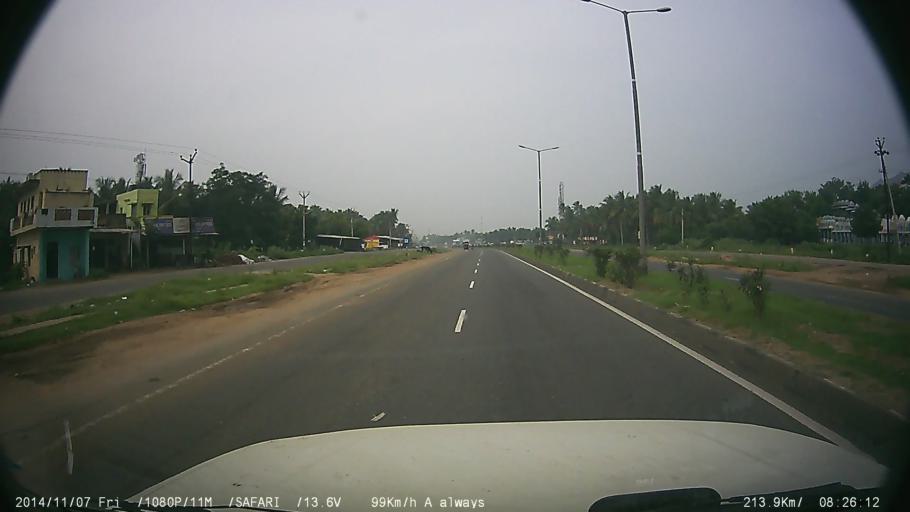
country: IN
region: Tamil Nadu
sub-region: Salem
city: Attayyampatti
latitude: 11.5957
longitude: 78.0823
